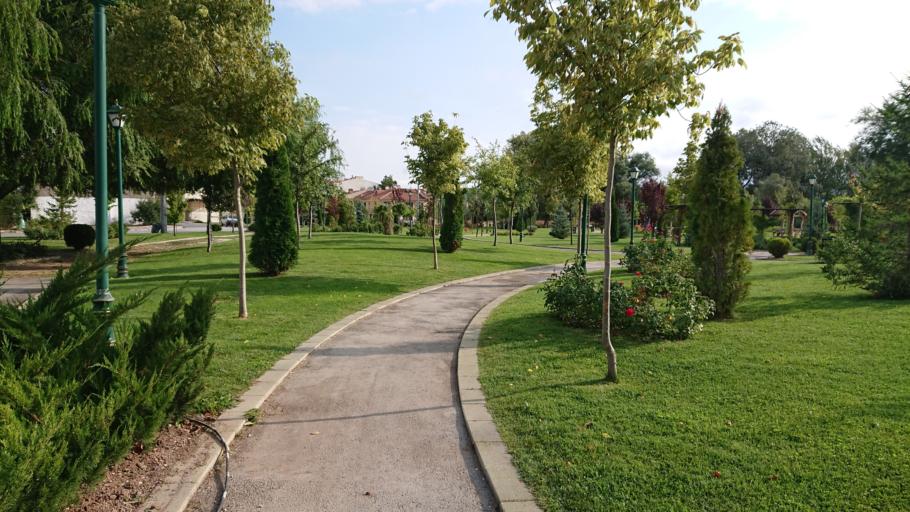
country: TR
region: Eskisehir
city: Eskisehir
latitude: 39.7631
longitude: 30.4869
